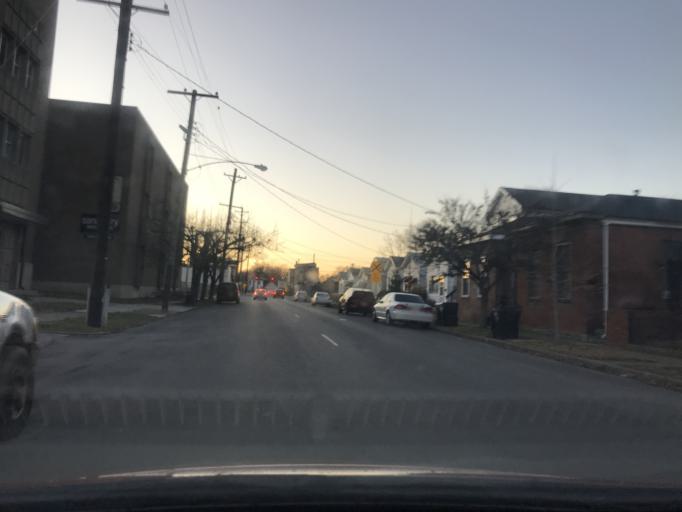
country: US
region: Kentucky
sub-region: Jefferson County
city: Louisville
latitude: 38.2340
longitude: -85.7377
